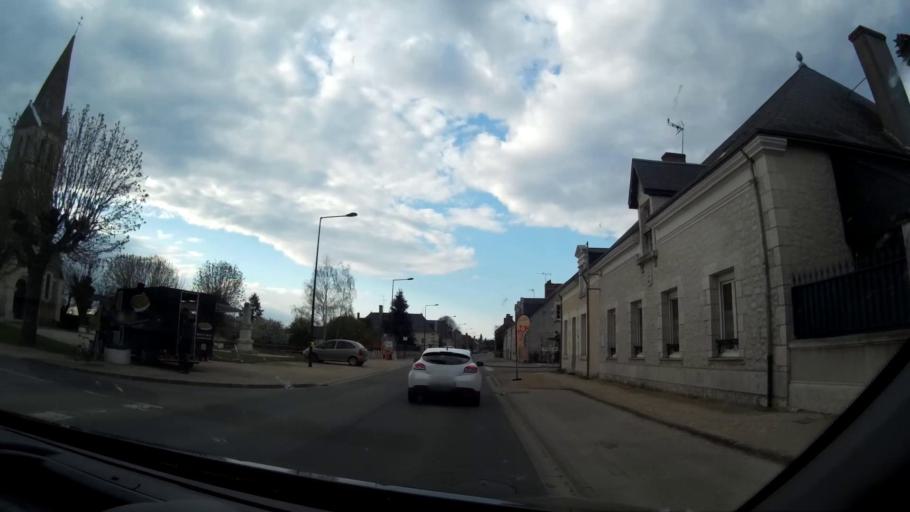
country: FR
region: Centre
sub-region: Departement du Loir-et-Cher
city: Cormeray
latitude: 47.4891
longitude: 1.4075
